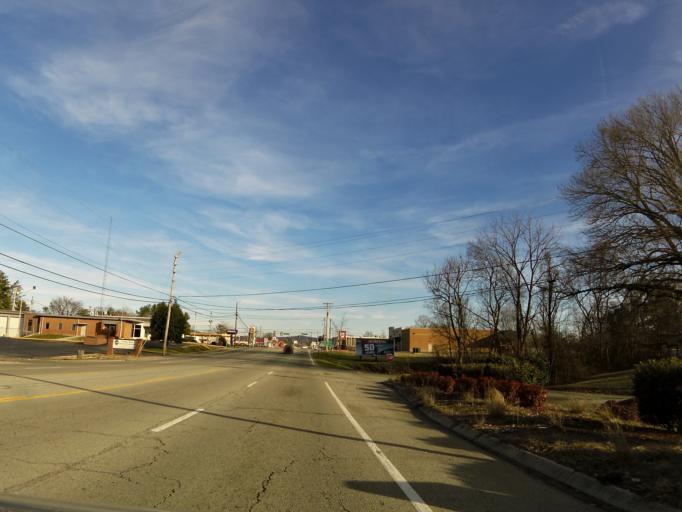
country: US
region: Tennessee
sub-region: White County
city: Sparta
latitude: 35.9330
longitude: -85.4784
